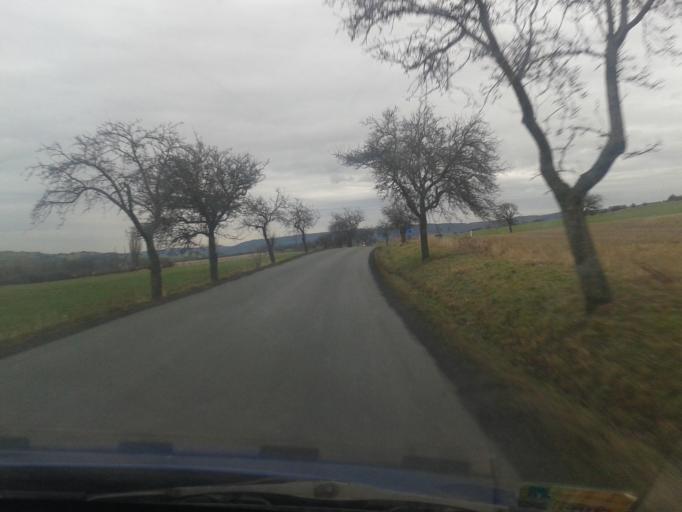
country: CZ
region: Central Bohemia
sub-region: Okres Beroun
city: Beroun
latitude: 49.9058
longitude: 14.1266
